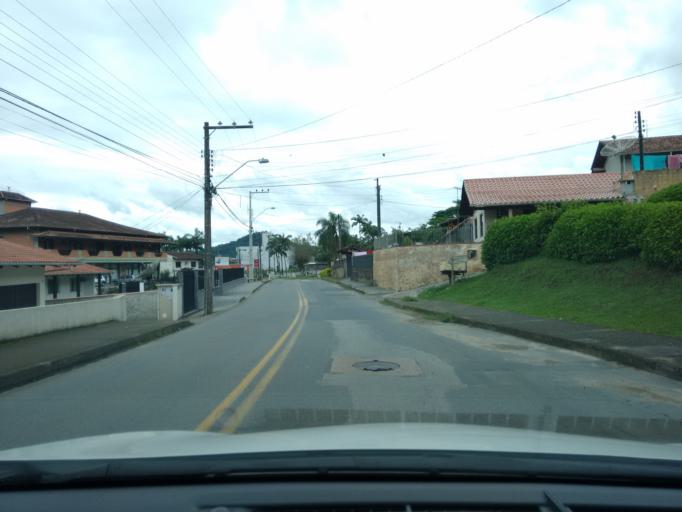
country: BR
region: Santa Catarina
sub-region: Blumenau
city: Blumenau
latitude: -26.8562
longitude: -49.1342
